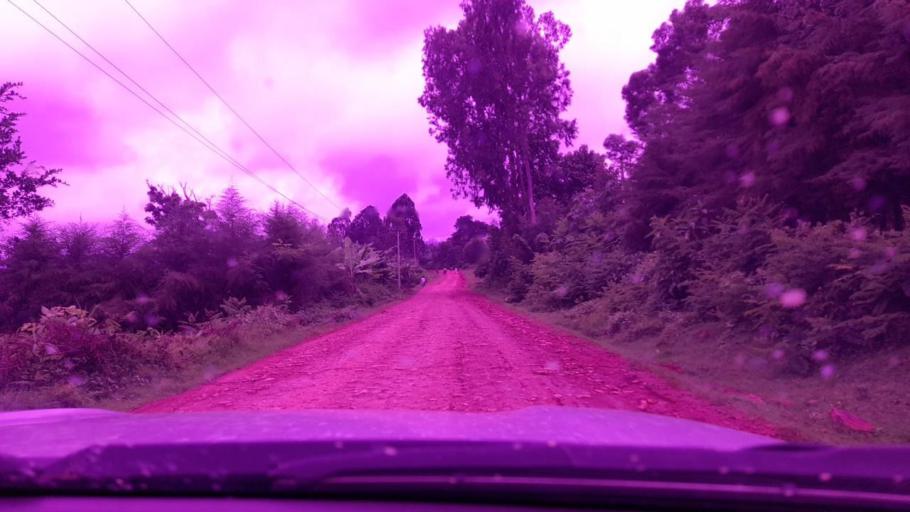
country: ET
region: Southern Nations, Nationalities, and People's Region
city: Bonga
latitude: 7.5479
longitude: 35.8734
